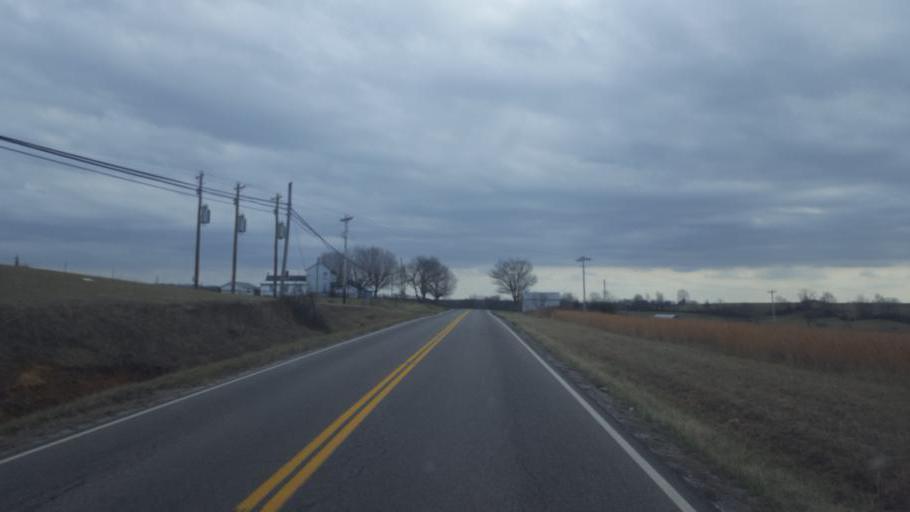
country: US
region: Ohio
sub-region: Jackson County
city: Oak Hill
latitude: 38.7993
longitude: -82.4008
